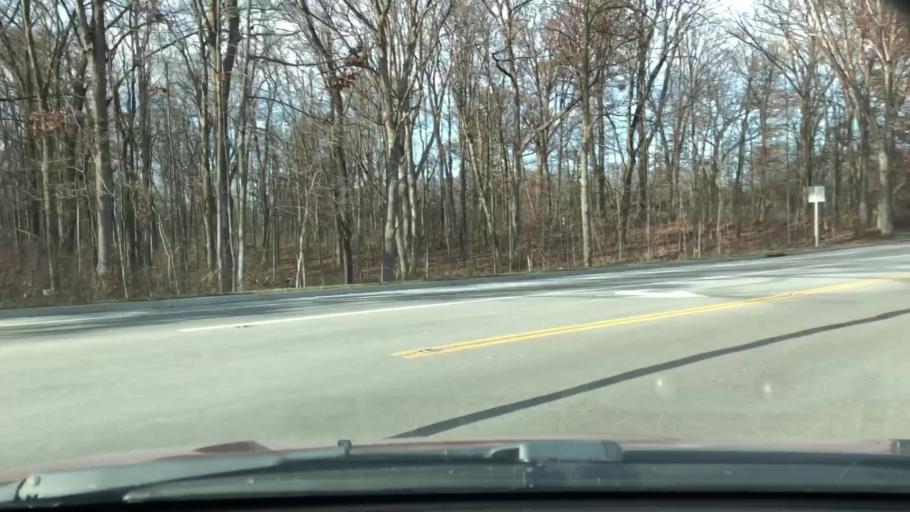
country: US
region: Ohio
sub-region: Greene County
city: Wright-Patterson AFB
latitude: 39.7651
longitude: -84.0759
